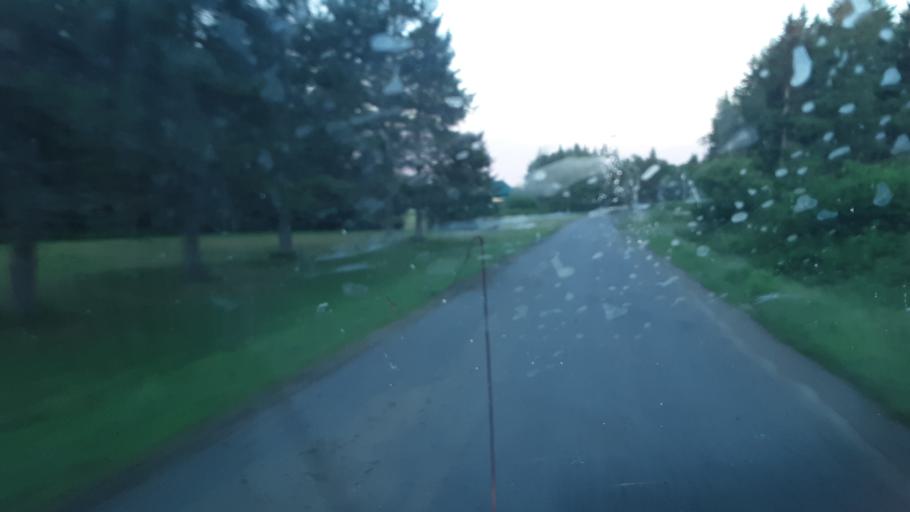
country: US
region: Maine
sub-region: Aroostook County
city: Caribou
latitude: 46.8709
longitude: -68.1229
